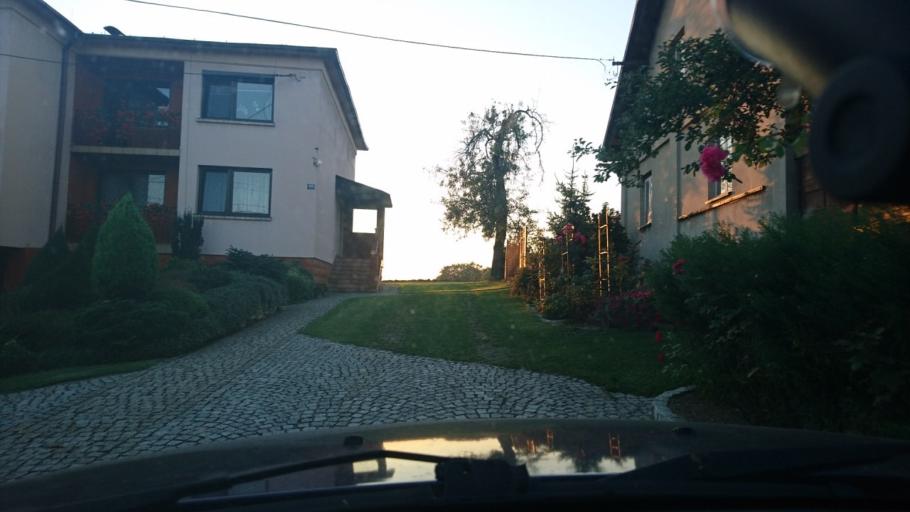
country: PL
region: Silesian Voivodeship
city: Janowice
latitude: 49.9026
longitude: 19.0817
